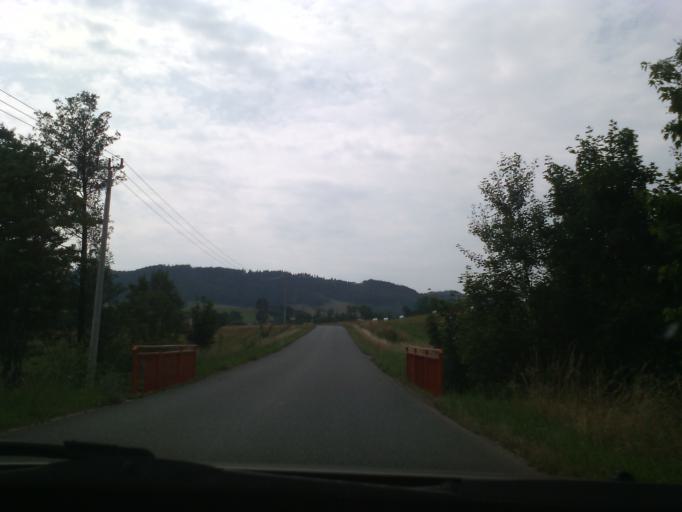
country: PL
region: Lower Silesian Voivodeship
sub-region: Powiat walbrzyski
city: Walbrzych
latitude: 50.7104
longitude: 16.2809
